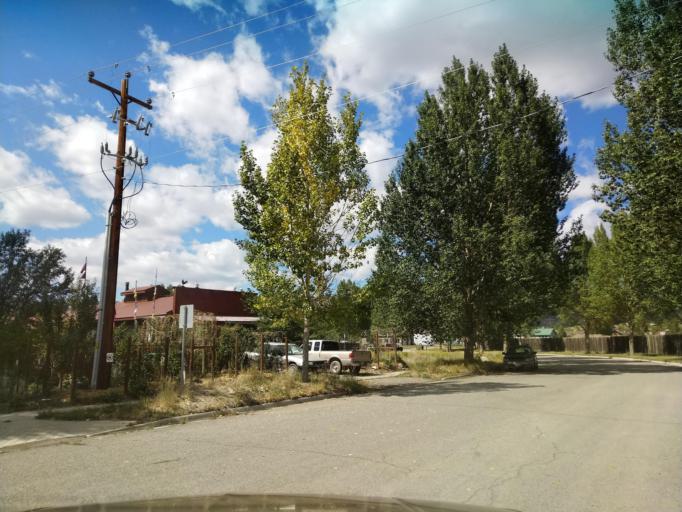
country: US
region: Colorado
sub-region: Ouray County
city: Ouray
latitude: 38.1555
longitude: -107.7563
